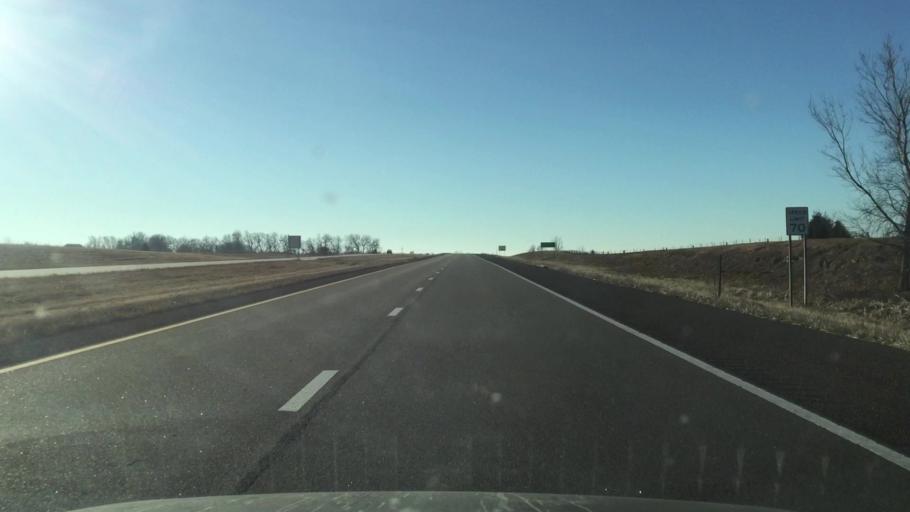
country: US
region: Kansas
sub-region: Miami County
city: Paola
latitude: 38.6133
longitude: -94.8361
